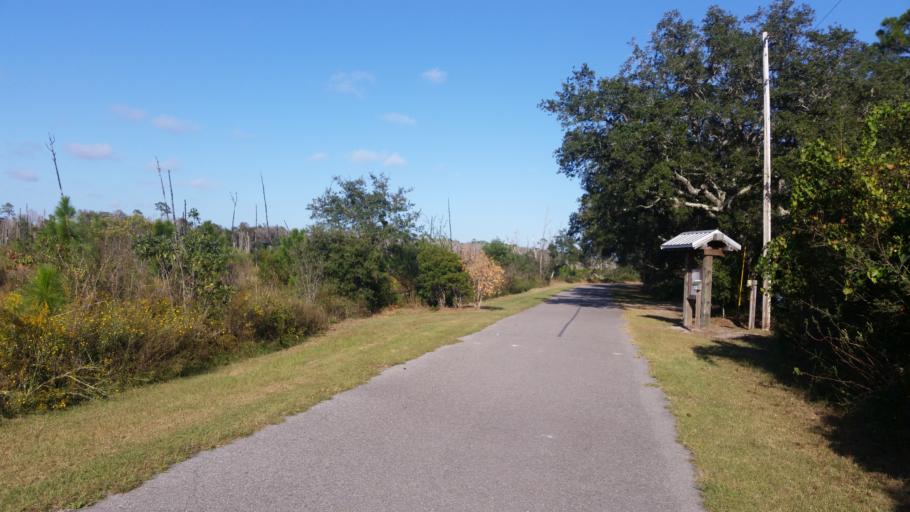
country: US
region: Alabama
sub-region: Baldwin County
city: Orange Beach
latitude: 30.2755
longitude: -87.6158
